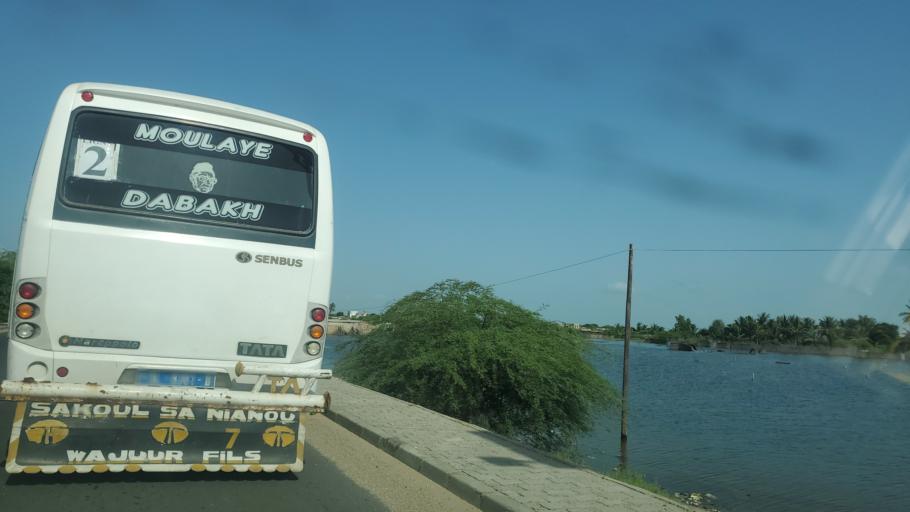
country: SN
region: Saint-Louis
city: Saint-Louis
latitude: 16.0360
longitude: -16.4656
